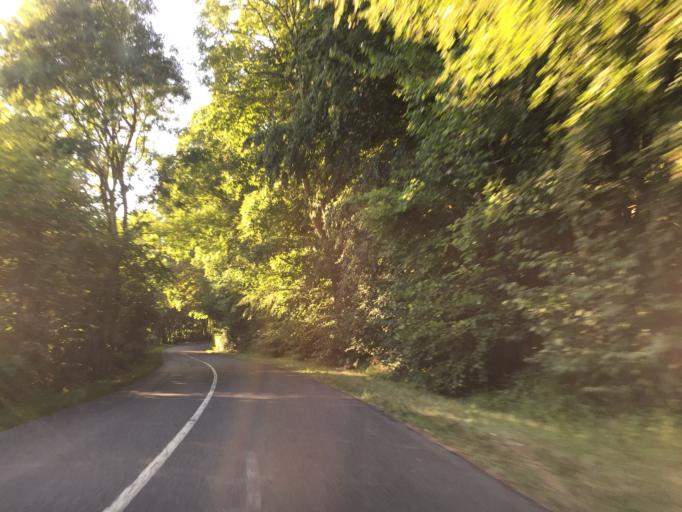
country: FR
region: Lower Normandy
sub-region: Departement du Calvados
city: Equemauville
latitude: 49.4020
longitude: 0.1811
